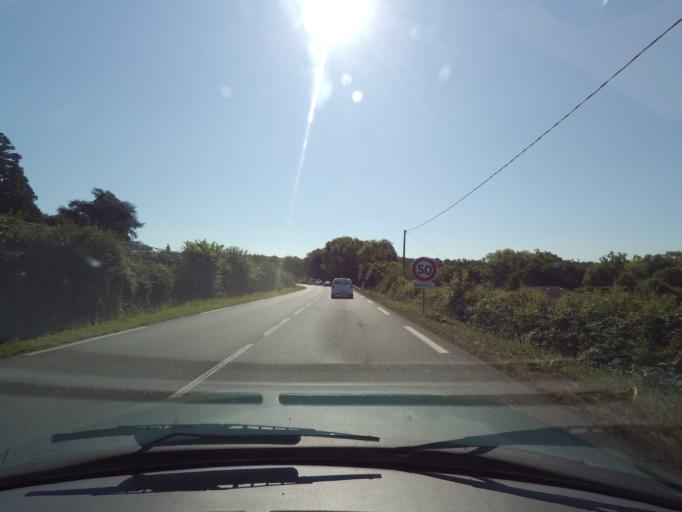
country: FR
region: Limousin
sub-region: Departement de la Haute-Vienne
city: Bussiere-Poitevine
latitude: 46.1664
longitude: 0.9549
